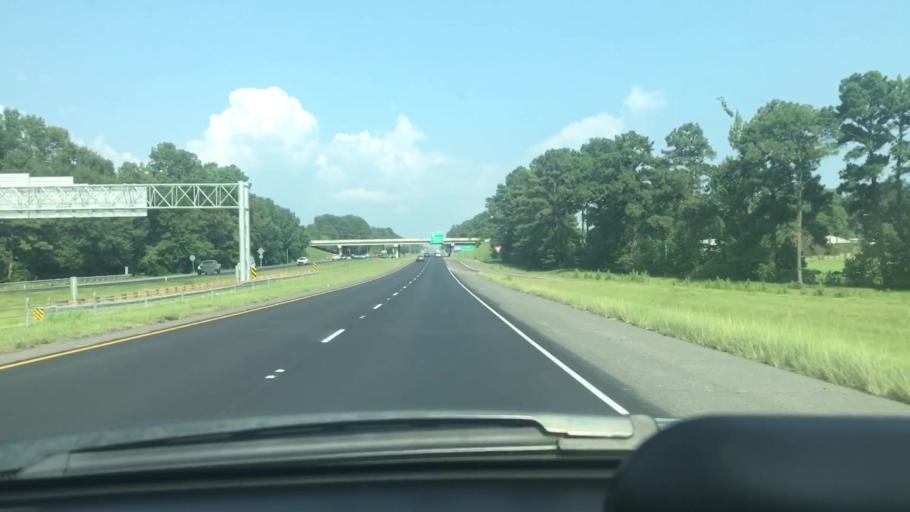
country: US
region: Louisiana
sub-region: Tangipahoa Parish
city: Hammond
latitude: 30.4789
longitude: -90.4862
